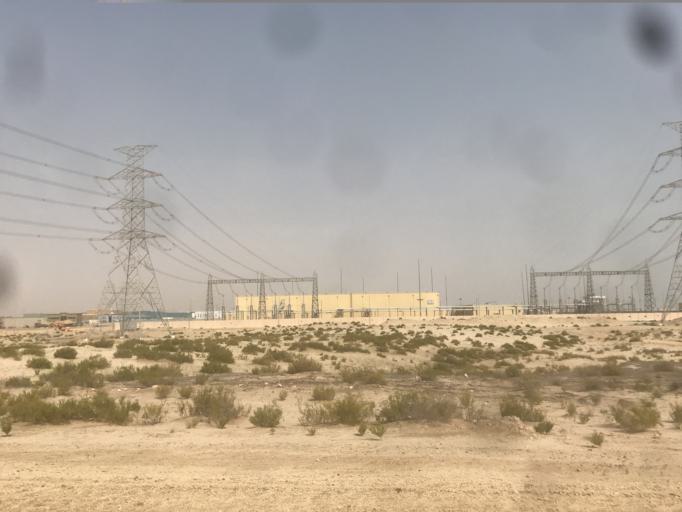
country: SA
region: Eastern Province
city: Abqaiq
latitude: 25.9108
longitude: 49.9610
